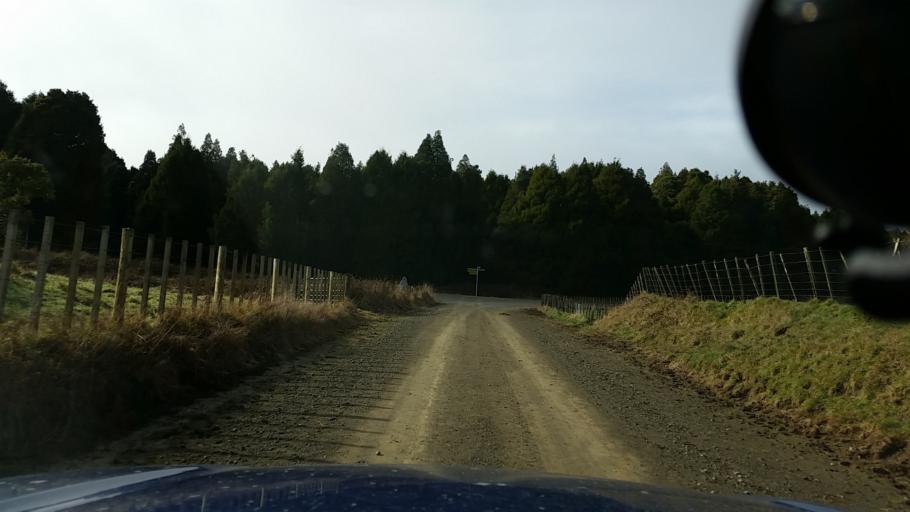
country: NZ
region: Taranaki
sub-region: New Plymouth District
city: Waitara
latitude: -38.9788
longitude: 174.7599
